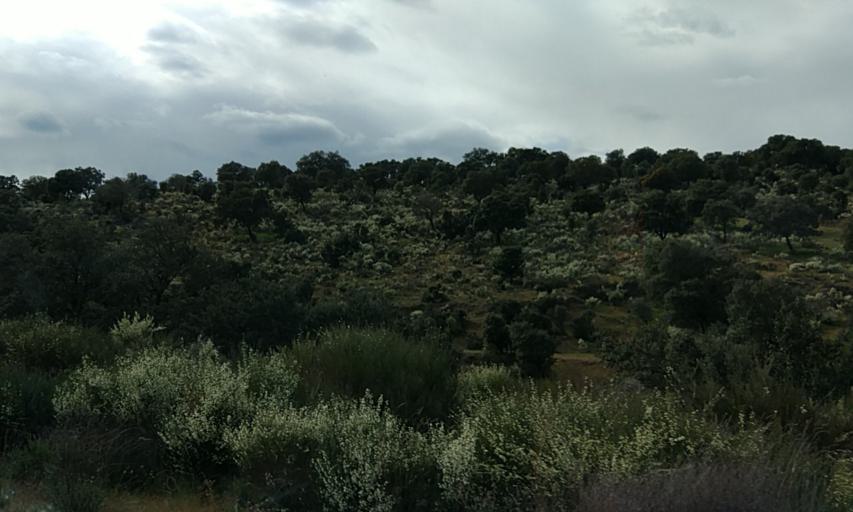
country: ES
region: Castille and Leon
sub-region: Provincia de Salamanca
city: Pastores
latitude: 40.5086
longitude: -6.5726
